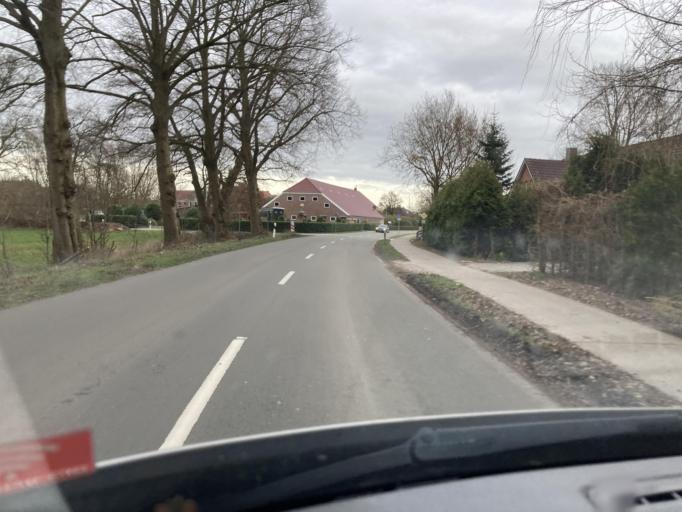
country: DE
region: Lower Saxony
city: Leer
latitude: 53.1673
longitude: 7.4450
